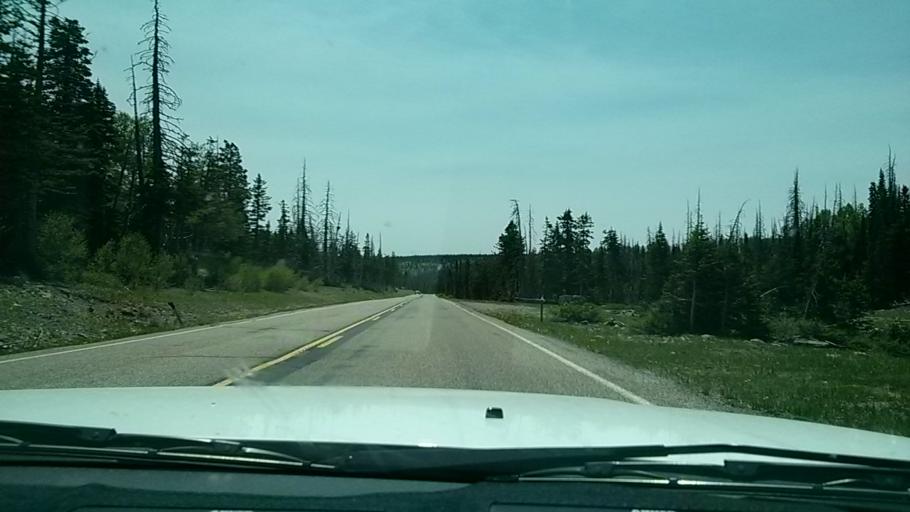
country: US
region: Utah
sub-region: Iron County
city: Cedar City
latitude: 37.5901
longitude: -112.8490
